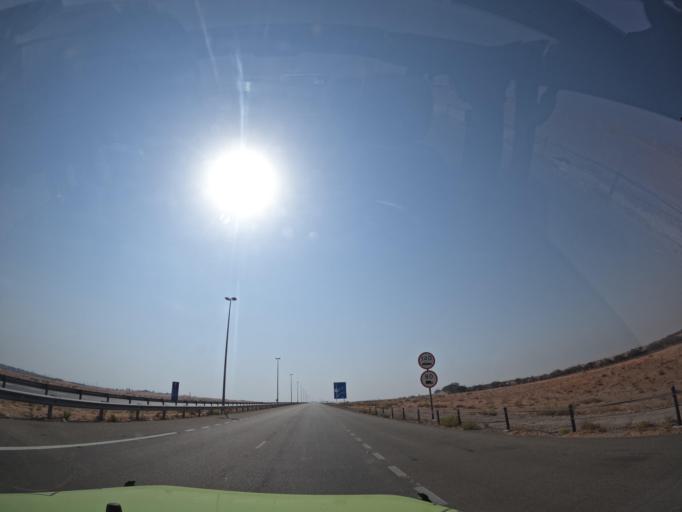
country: OM
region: Al Buraimi
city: Al Buraymi
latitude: 24.4021
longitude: 55.7124
